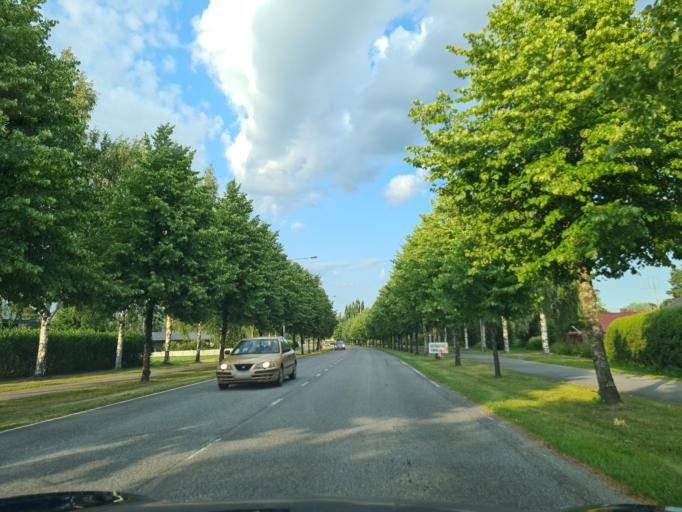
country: FI
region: Southern Ostrobothnia
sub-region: Seinaejoki
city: Lapua
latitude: 62.9685
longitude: 22.9903
